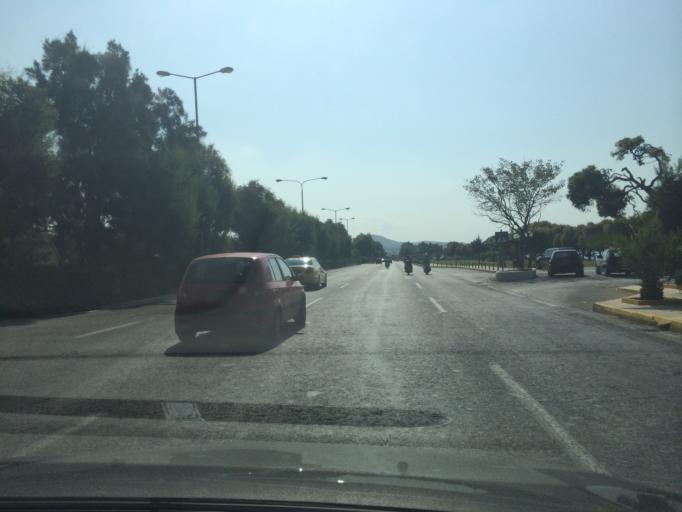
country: GR
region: Attica
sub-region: Nomarchia Anatolikis Attikis
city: Voula
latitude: 37.8434
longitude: 23.7571
